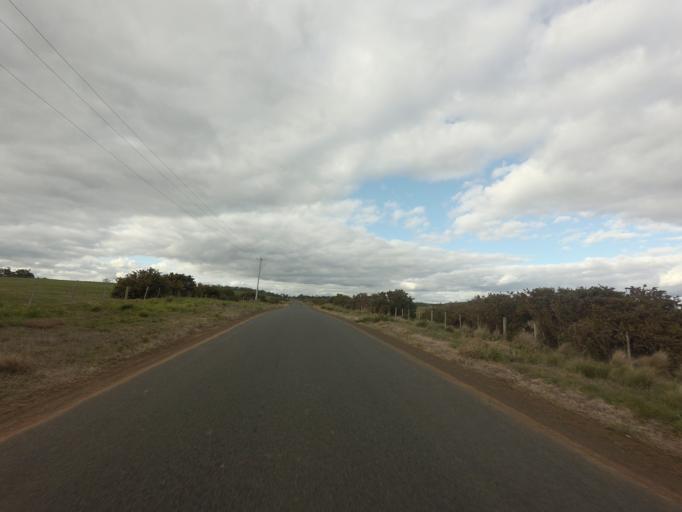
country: AU
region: Tasmania
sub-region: Northern Midlands
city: Evandale
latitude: -41.9053
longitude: 147.3952
